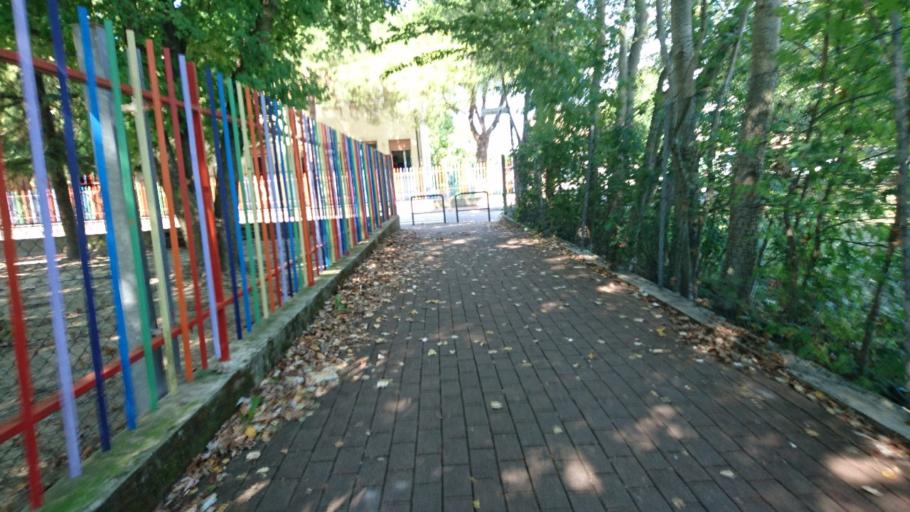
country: IT
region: Veneto
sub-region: Provincia di Venezia
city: Campalto
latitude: 45.5056
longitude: 12.2671
